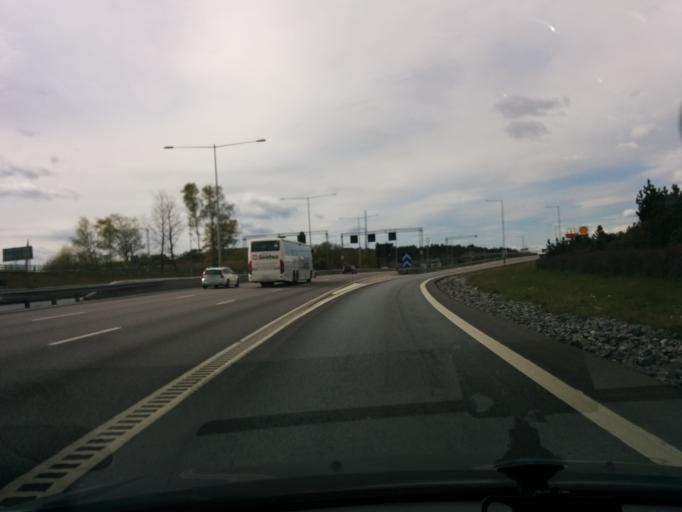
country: SE
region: Stockholm
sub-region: Botkyrka Kommun
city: Eriksberg
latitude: 59.2402
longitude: 17.8339
